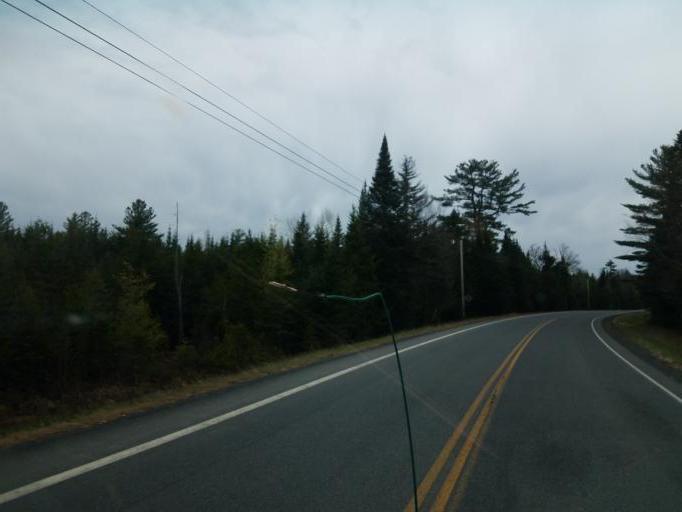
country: US
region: Maine
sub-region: Penobscot County
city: Patten
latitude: 46.2871
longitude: -68.3574
